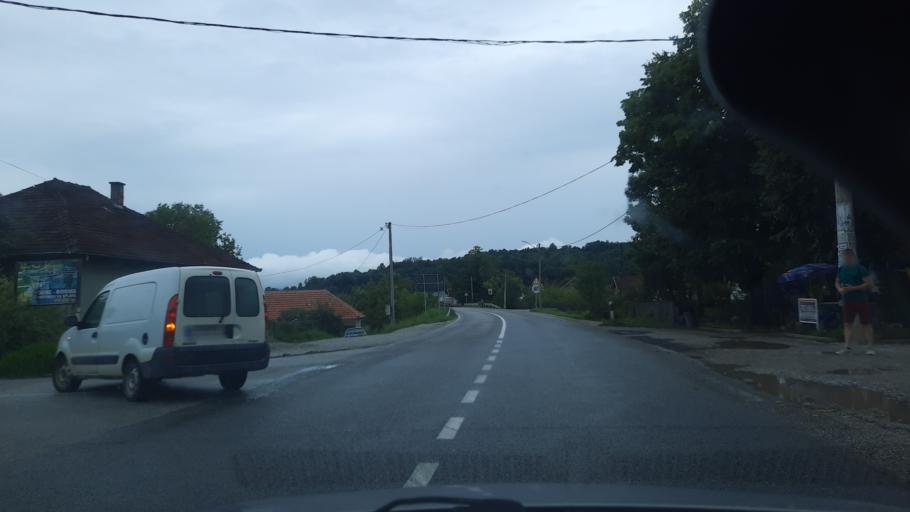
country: RS
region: Central Serbia
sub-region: Raski Okrug
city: Kraljevo
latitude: 43.7255
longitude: 20.7992
